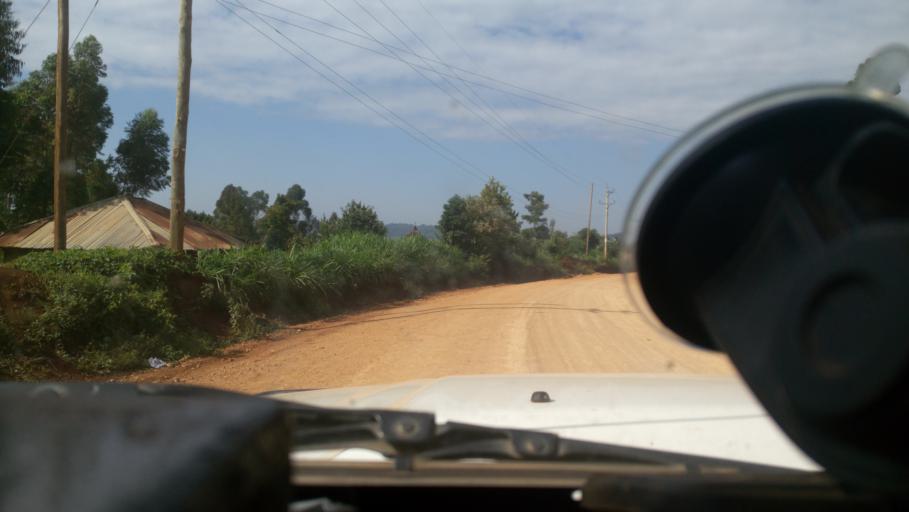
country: KE
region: Nyamira District
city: Nyamira
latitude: -0.6770
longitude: 34.9141
